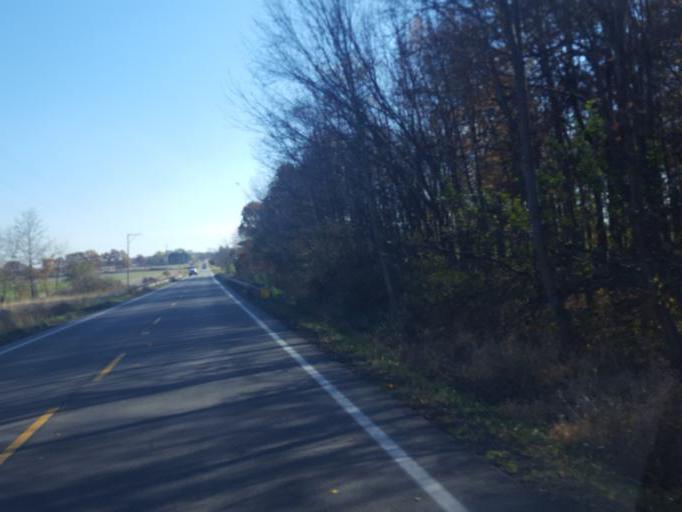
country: US
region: Ohio
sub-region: Wayne County
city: West Salem
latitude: 40.9896
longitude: -82.2214
